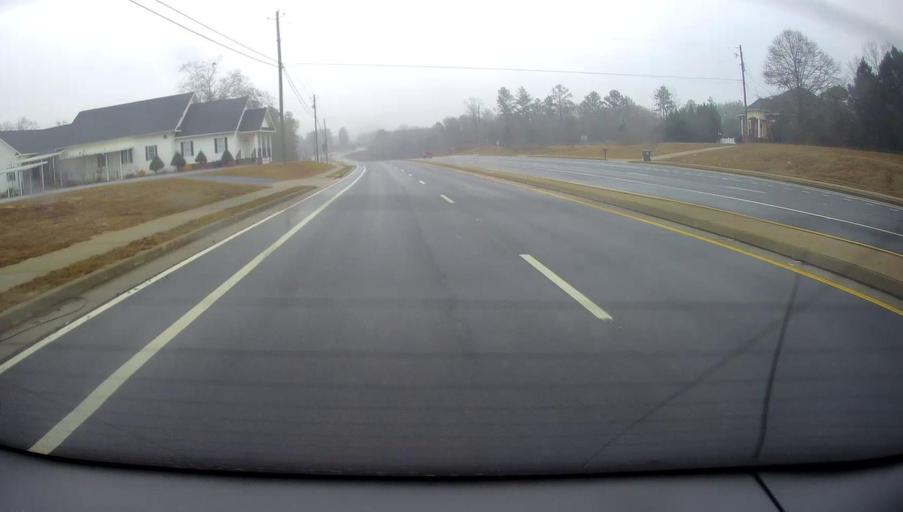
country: US
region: Georgia
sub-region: Peach County
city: Byron
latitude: 32.7169
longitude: -83.7111
